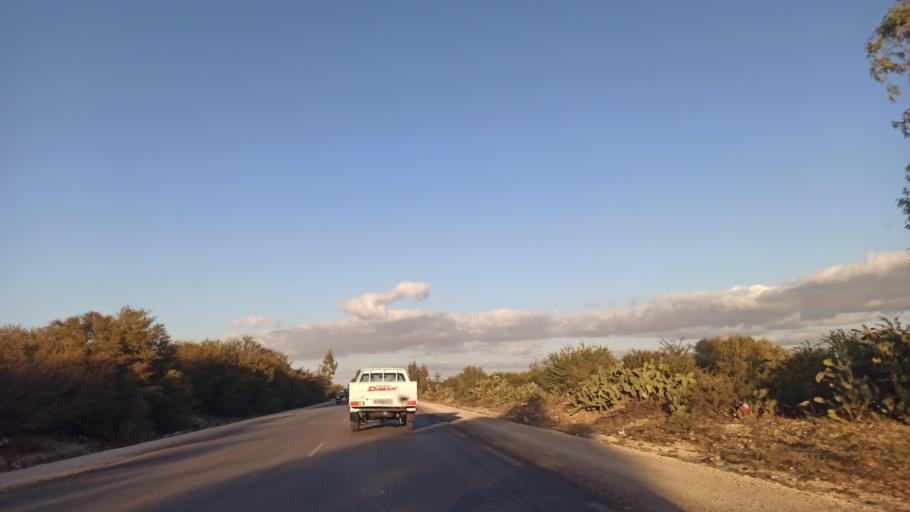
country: TN
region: Al Qayrawan
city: Sbikha
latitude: 35.8576
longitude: 10.2031
